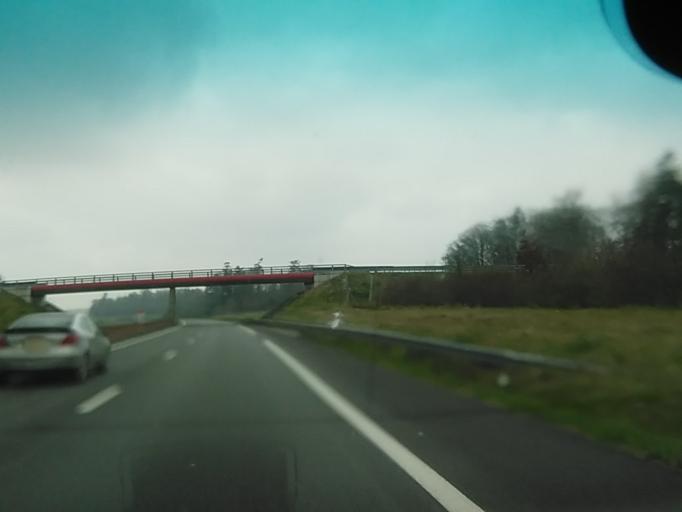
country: FR
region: Lower Normandy
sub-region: Departement de l'Orne
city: Gace
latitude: 48.8621
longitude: 0.3806
